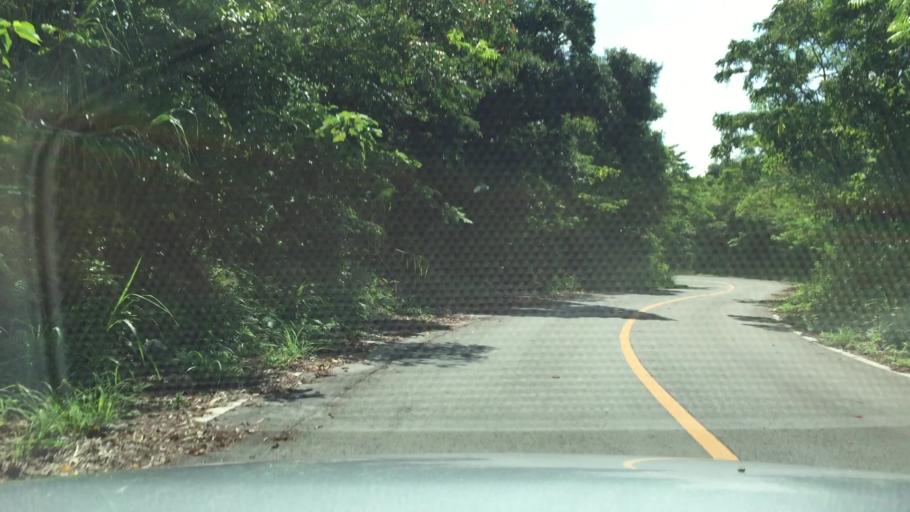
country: JP
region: Okinawa
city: Ishigaki
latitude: 24.3840
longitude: 124.1680
